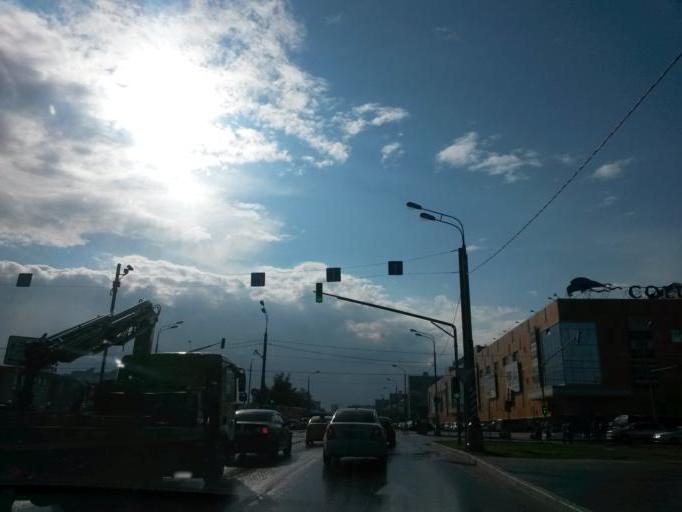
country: RU
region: Moscow
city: Chertanovo Yuzhnoye
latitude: 55.6102
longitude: 37.6092
